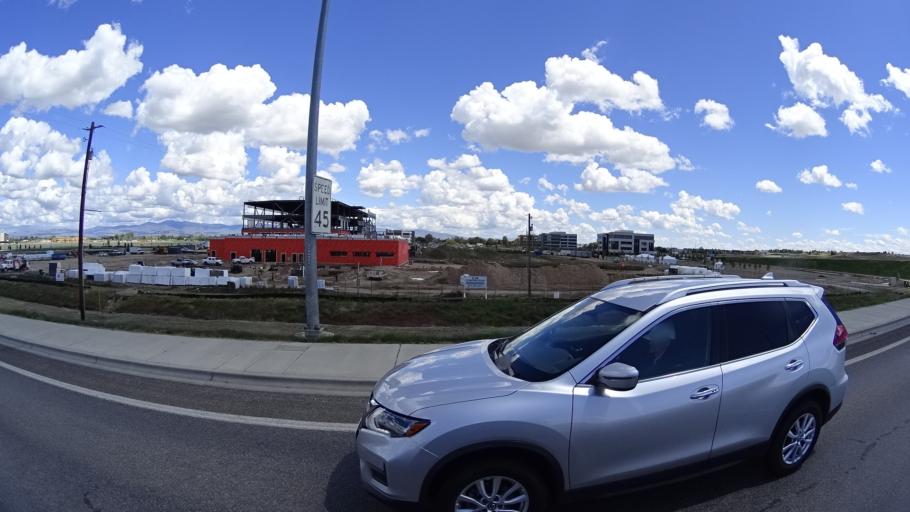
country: US
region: Idaho
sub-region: Ada County
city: Meridian
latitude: 43.5962
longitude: -116.4341
